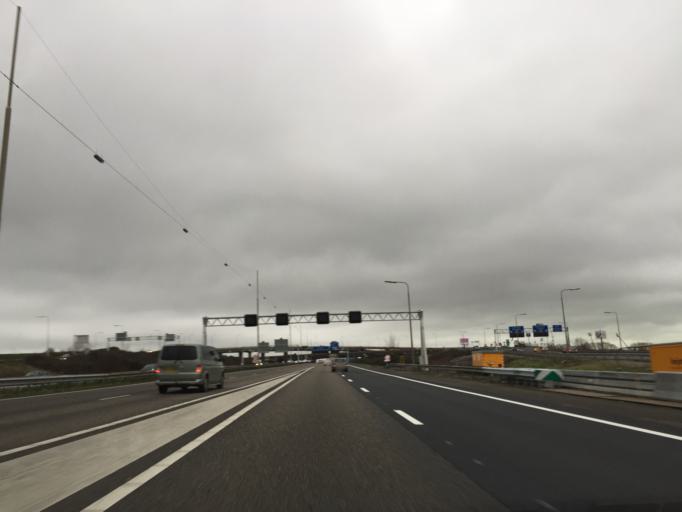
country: NL
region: South Holland
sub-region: Gemeente Den Haag
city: Ypenburg
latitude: 52.0579
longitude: 4.3709
